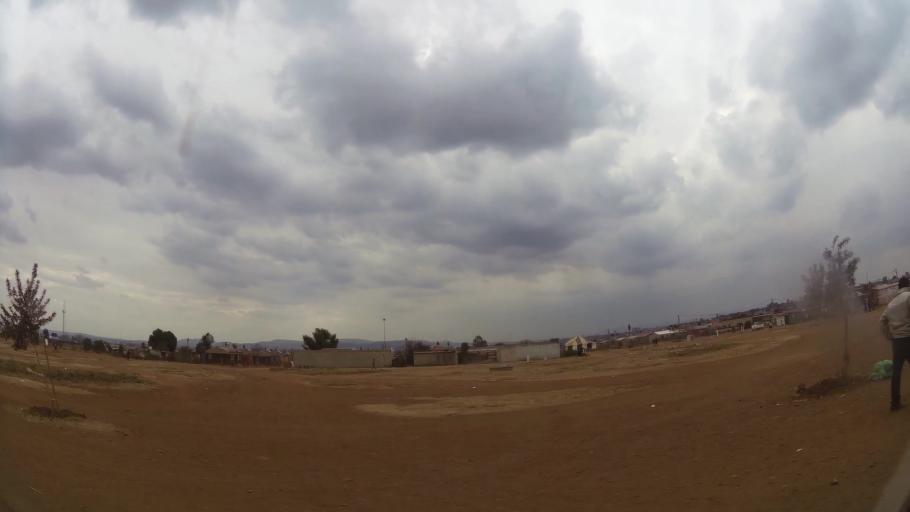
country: ZA
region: Gauteng
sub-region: Ekurhuleni Metropolitan Municipality
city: Germiston
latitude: -26.3901
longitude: 28.1346
